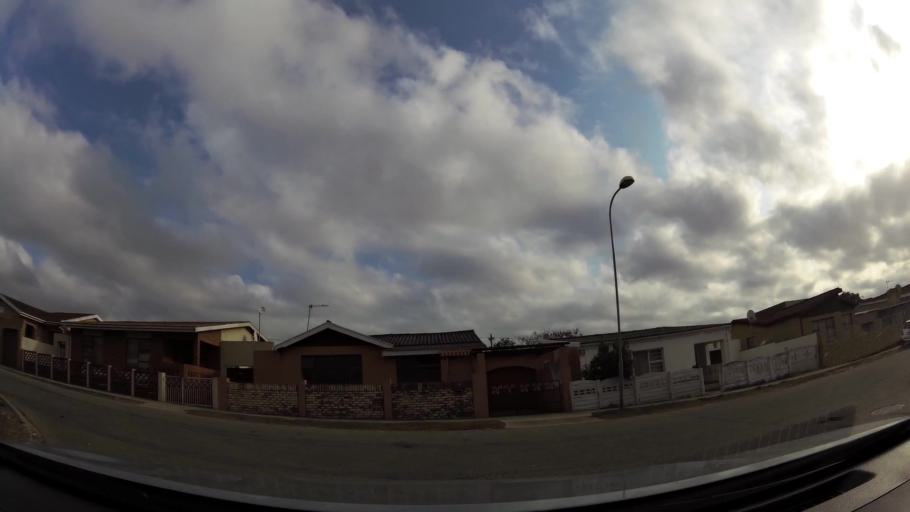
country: ZA
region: Eastern Cape
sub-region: Nelson Mandela Bay Metropolitan Municipality
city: Port Elizabeth
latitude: -33.9148
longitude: 25.5525
